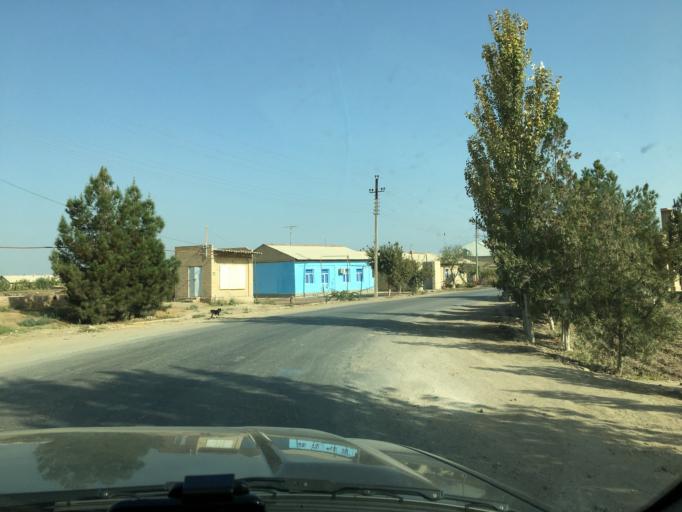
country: TM
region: Lebap
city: Atamyrat
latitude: 37.8344
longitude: 65.1864
